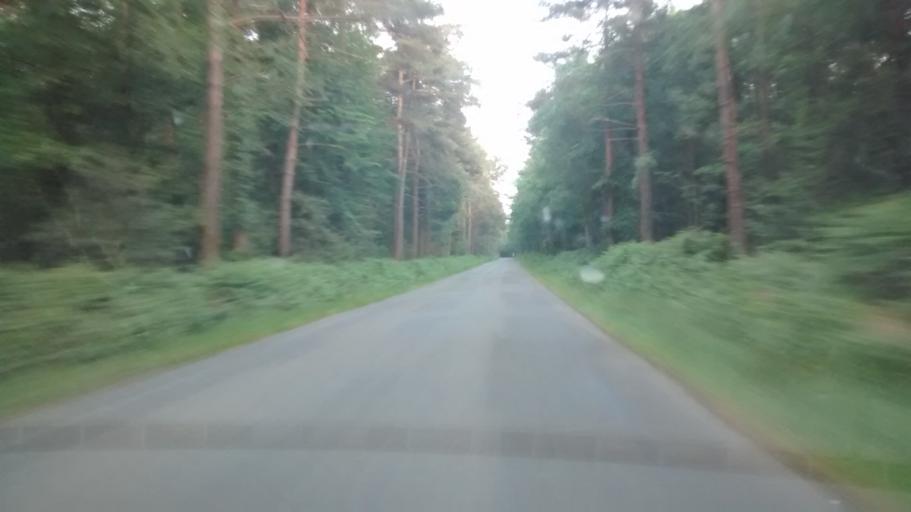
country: FR
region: Brittany
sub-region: Departement d'Ille-et-Vilaine
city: Paimpont
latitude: 48.0028
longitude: -2.1541
